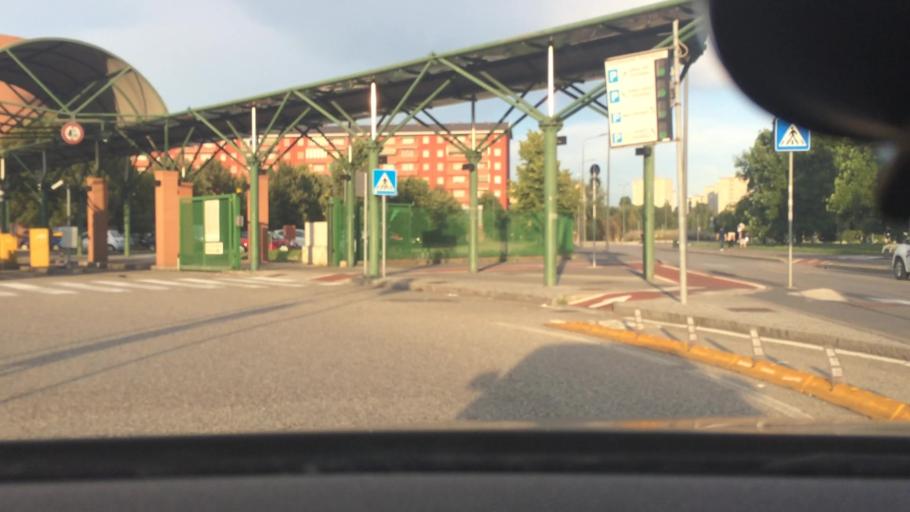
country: IT
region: Lombardy
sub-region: Citta metropolitana di Milano
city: Pero
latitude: 45.5053
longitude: 9.0939
